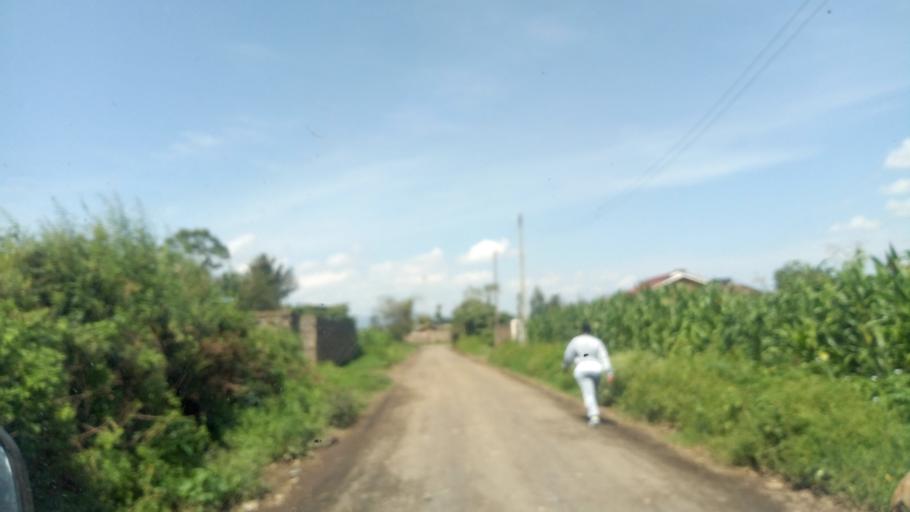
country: KE
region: Nakuru
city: Nakuru
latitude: -0.2779
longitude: 36.1160
